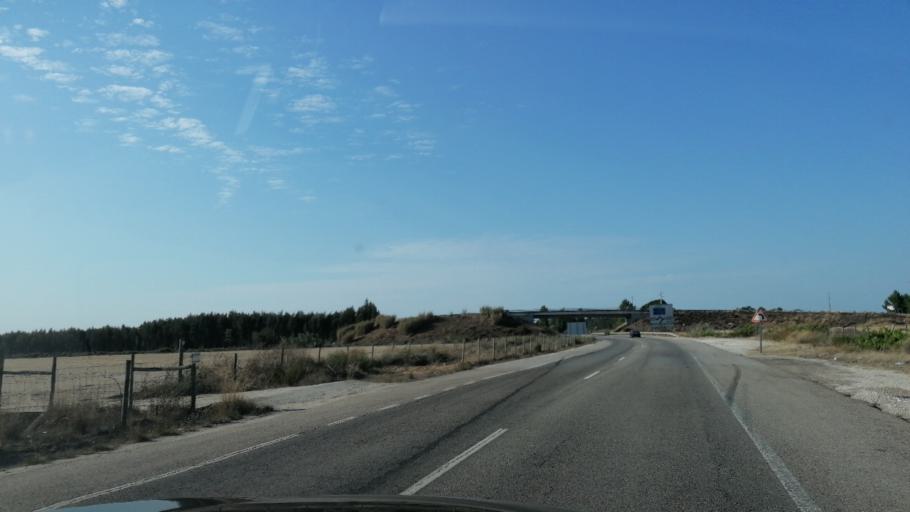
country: PT
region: Santarem
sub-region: Almeirim
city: Almeirim
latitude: 39.1707
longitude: -8.6206
